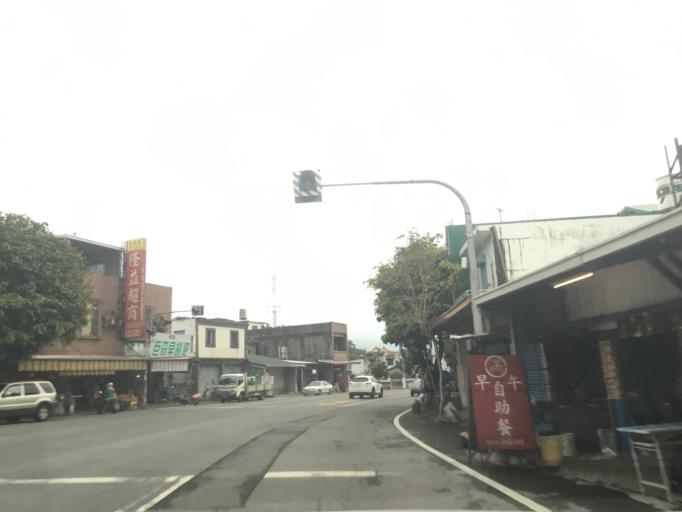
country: TW
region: Taiwan
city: Taitung City
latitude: 22.7626
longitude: 121.0497
